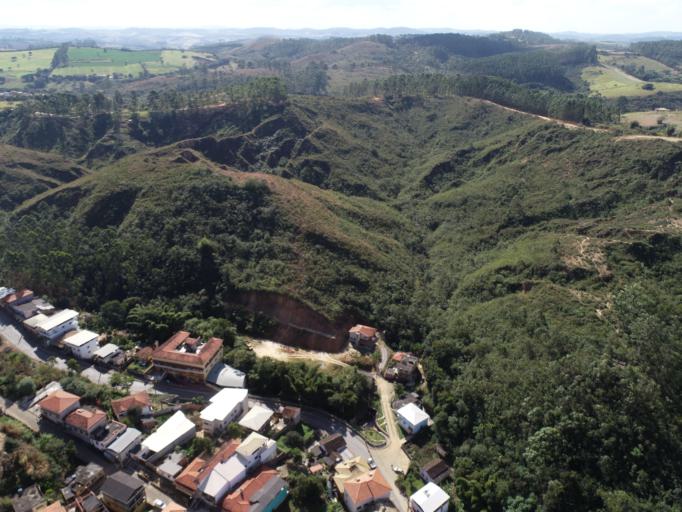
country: BR
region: Minas Gerais
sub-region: Tiradentes
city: Tiradentes
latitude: -21.0571
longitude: -44.0812
